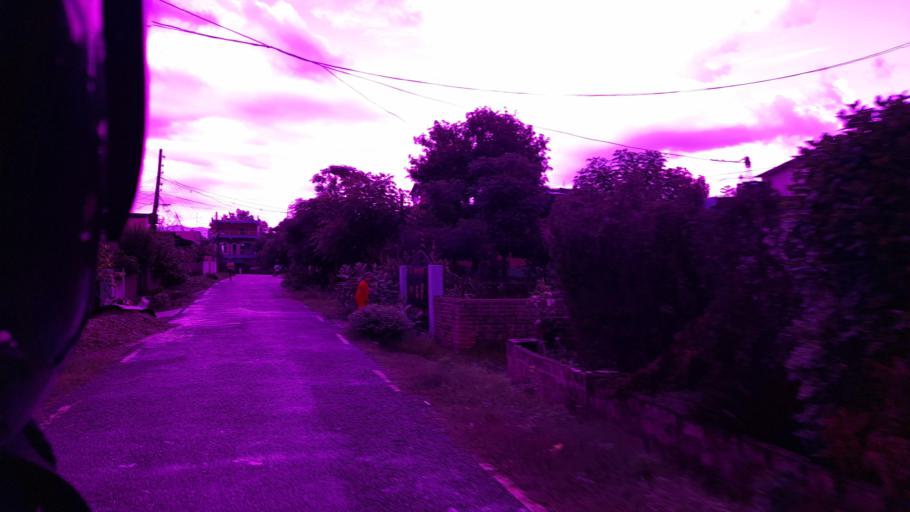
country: NP
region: Mid Western
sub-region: Bheri Zone
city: Nepalgunj
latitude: 28.1945
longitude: 81.6978
